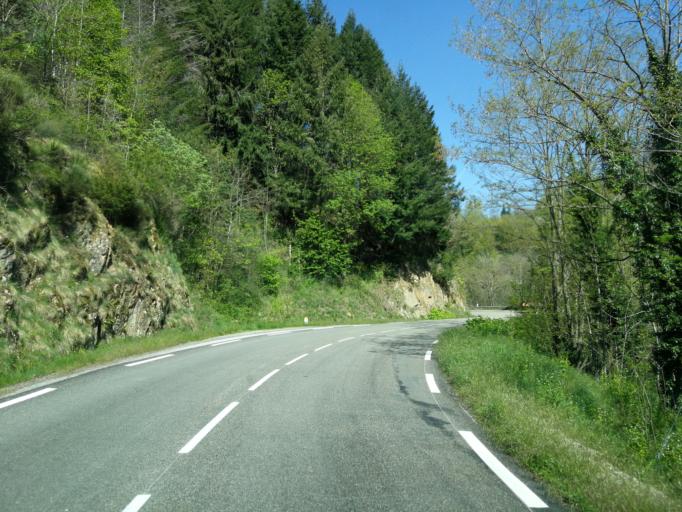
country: FR
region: Rhone-Alpes
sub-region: Departement de l'Ardeche
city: Le Cheylard
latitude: 44.9039
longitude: 4.4835
